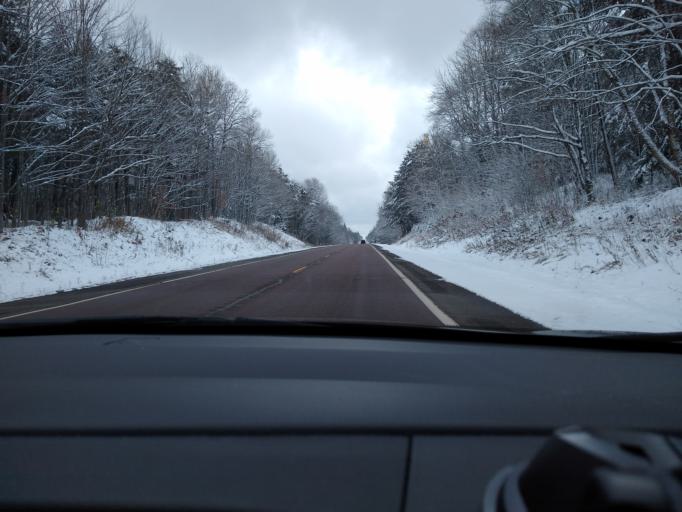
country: US
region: Wisconsin
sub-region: Vilas County
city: Eagle River
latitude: 46.2210
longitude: -89.0567
